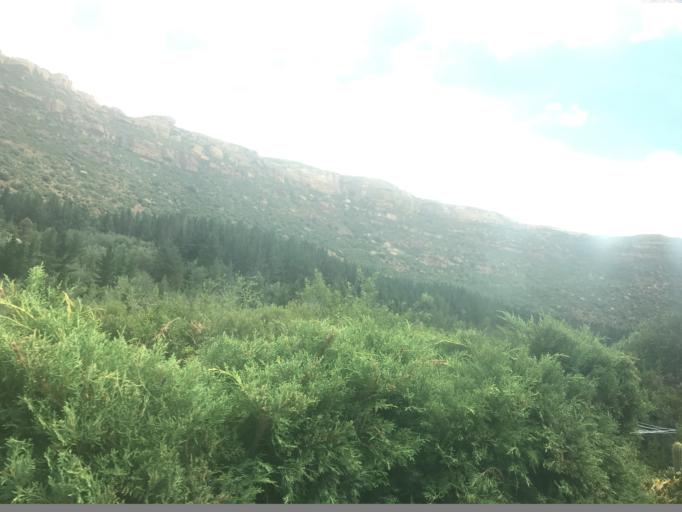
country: LS
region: Maseru
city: Nako
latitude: -29.6328
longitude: 27.5134
